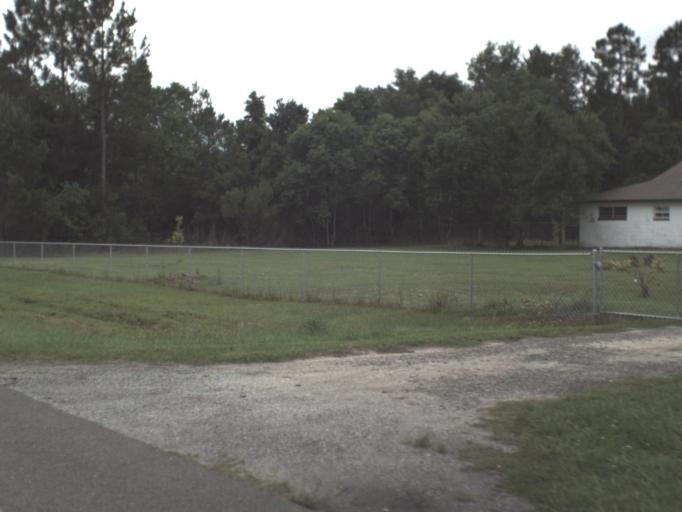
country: US
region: Florida
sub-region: Bradford County
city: Starke
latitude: 29.8849
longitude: -82.0827
